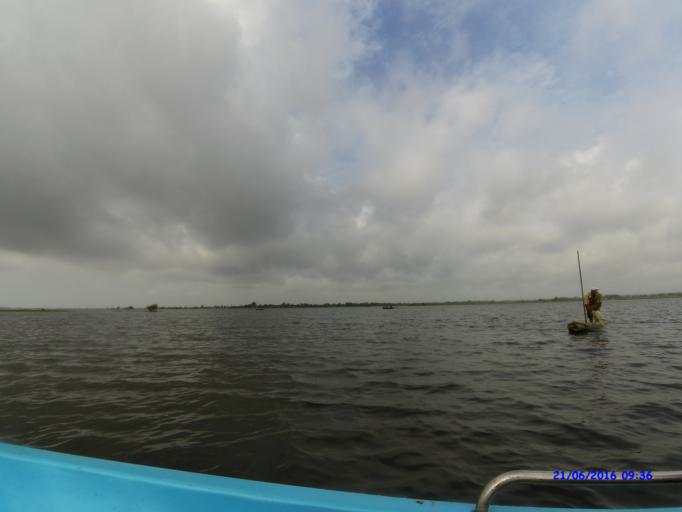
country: BJ
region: Mono
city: Come
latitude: 6.4254
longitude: 1.9300
